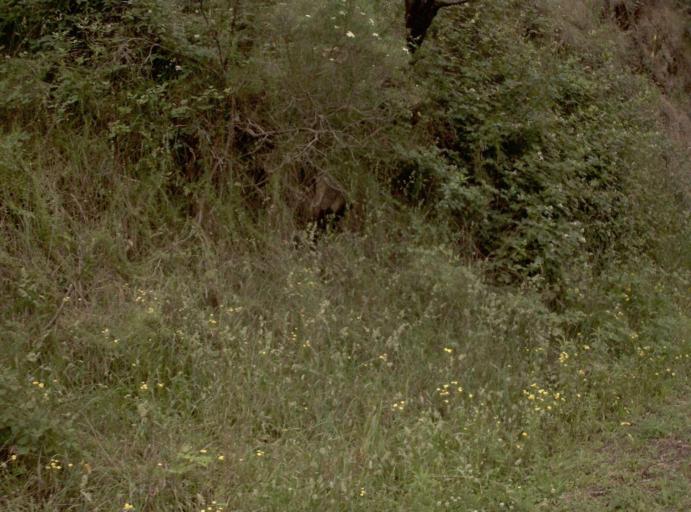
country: AU
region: Victoria
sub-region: East Gippsland
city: Bairnsdale
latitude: -37.4545
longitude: 147.2514
